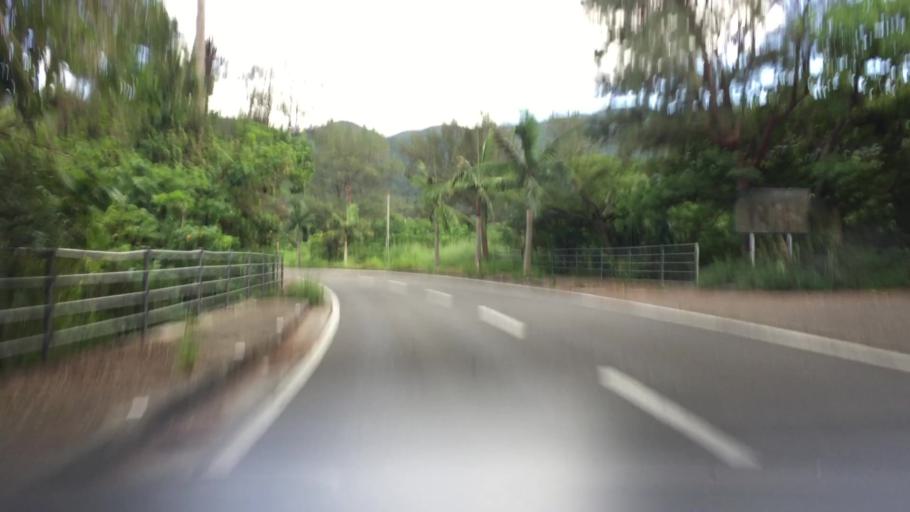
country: JP
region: Okinawa
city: Ishigaki
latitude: 24.4450
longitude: 124.1356
